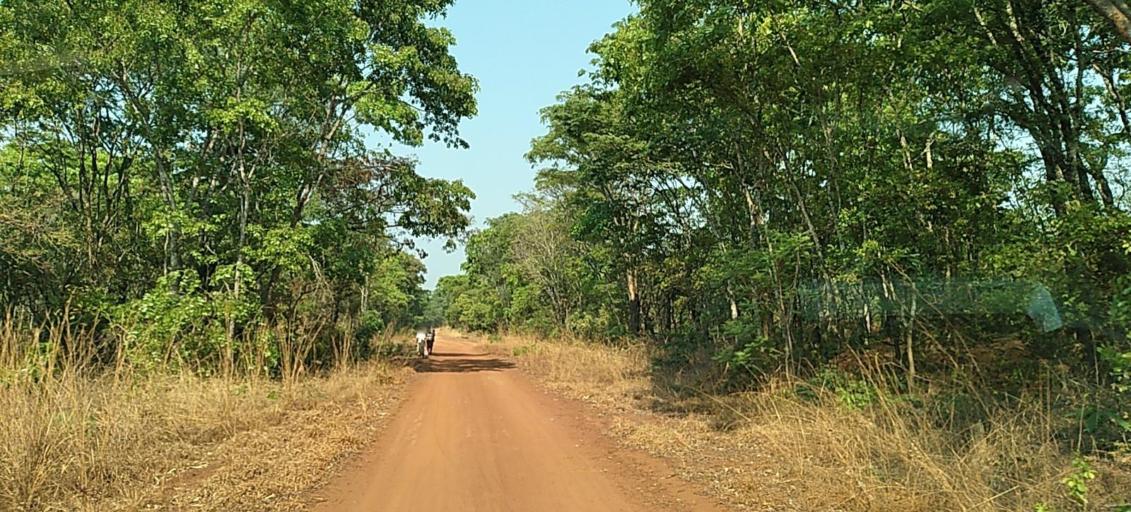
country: ZM
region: Copperbelt
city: Chingola
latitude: -12.8809
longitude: 27.4323
